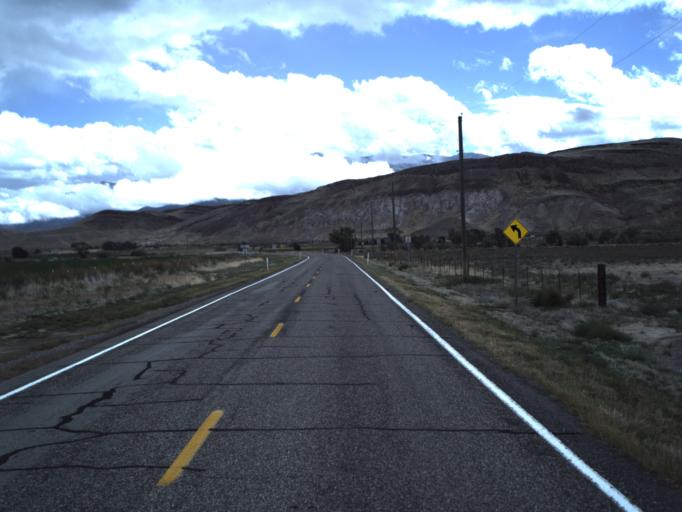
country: US
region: Utah
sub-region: Sevier County
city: Monroe
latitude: 38.6242
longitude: -112.2111
